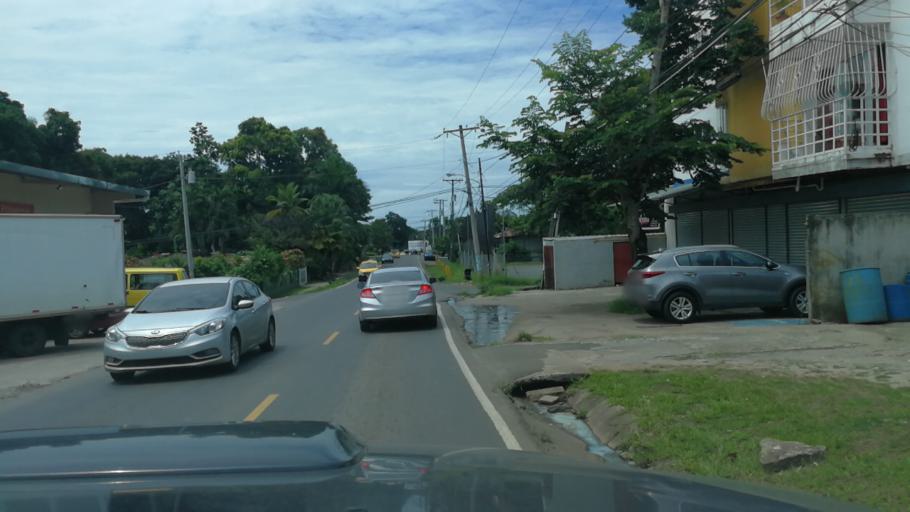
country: PA
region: Panama
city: Tocumen
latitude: 9.0735
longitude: -79.4276
